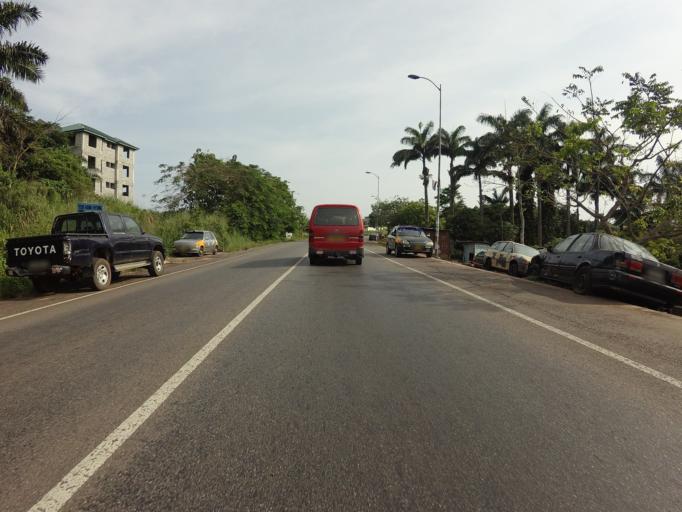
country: GH
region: Eastern
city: Aburi
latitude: 5.8334
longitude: -0.1827
